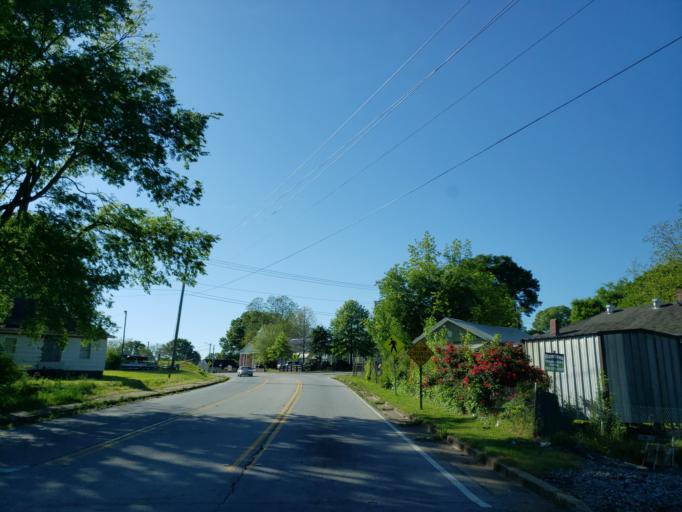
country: US
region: Georgia
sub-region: Polk County
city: Cedartown
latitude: 34.0037
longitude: -85.2499
